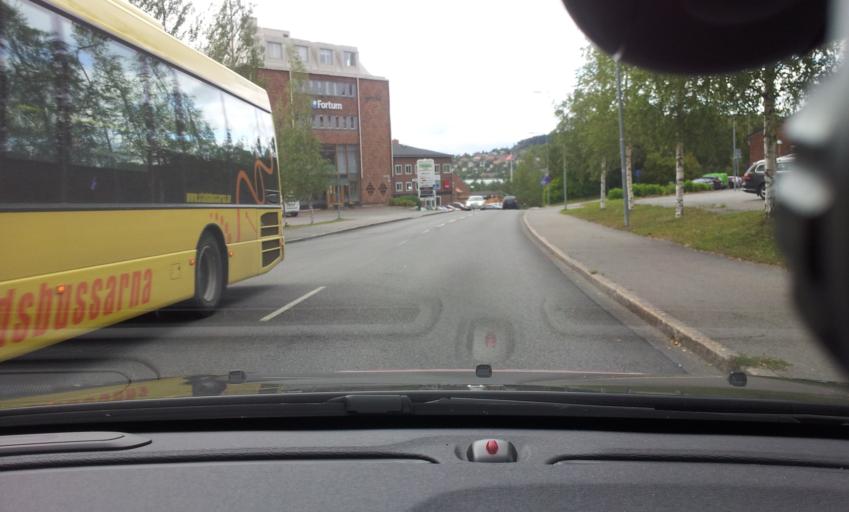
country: SE
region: Jaemtland
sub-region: OEstersunds Kommun
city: Ostersund
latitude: 63.1695
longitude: 14.6424
